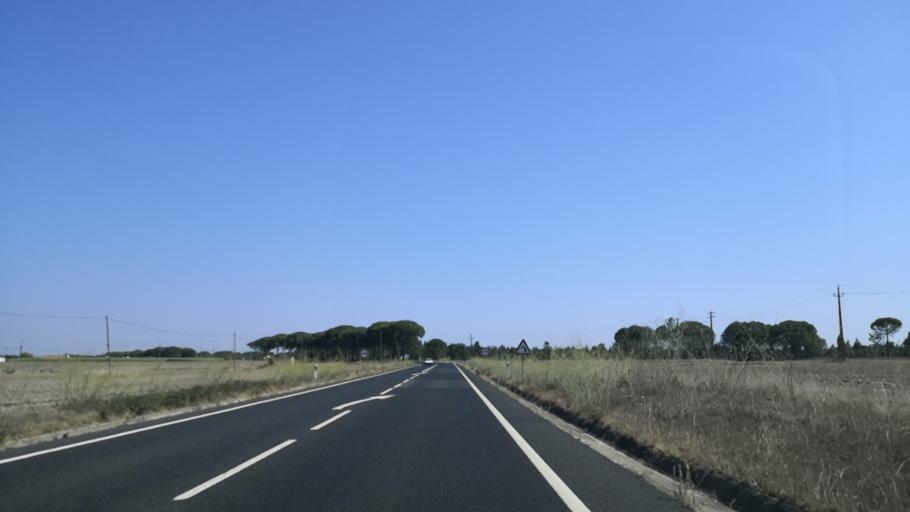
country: PT
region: Santarem
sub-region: Benavente
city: Poceirao
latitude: 38.7256
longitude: -8.6430
